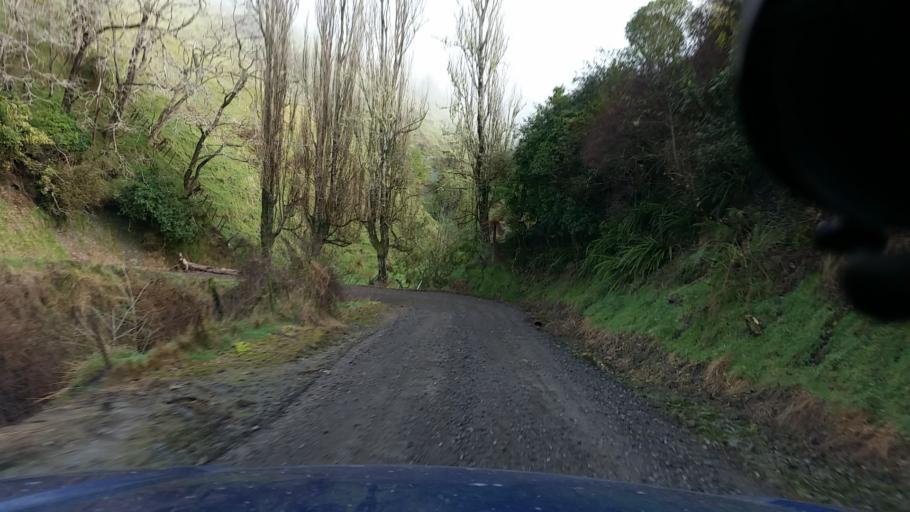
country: NZ
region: Taranaki
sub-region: New Plymouth District
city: Waitara
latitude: -38.9994
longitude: 174.7668
